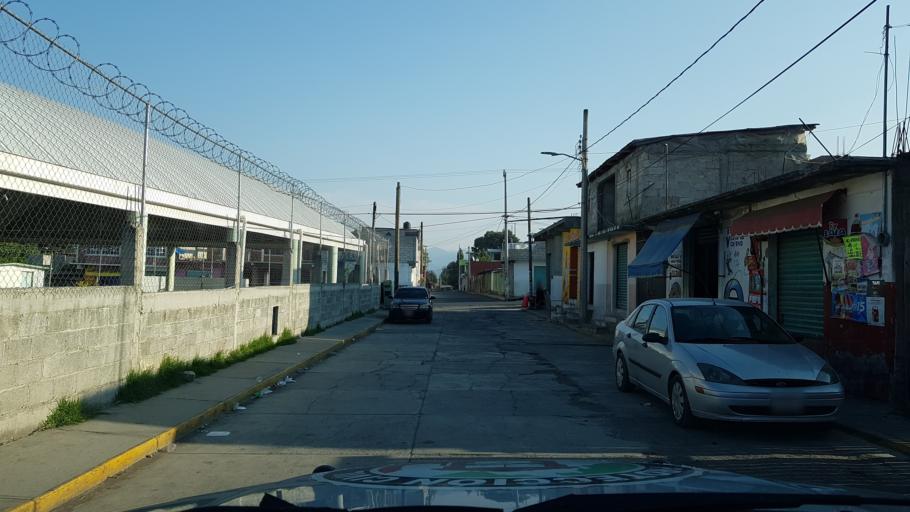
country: MX
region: Mexico
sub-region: Amecameca
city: San Diego Huehuecalco
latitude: 19.0835
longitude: -98.7369
